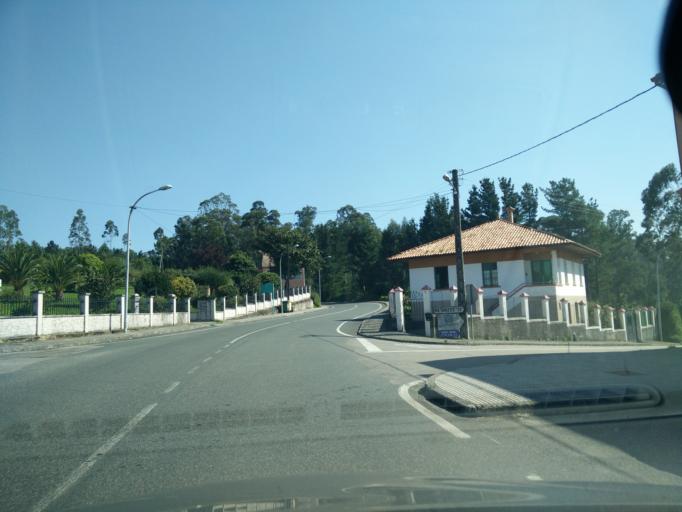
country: ES
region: Galicia
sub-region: Provincia da Coruna
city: Mino
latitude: 43.3402
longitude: -8.1547
